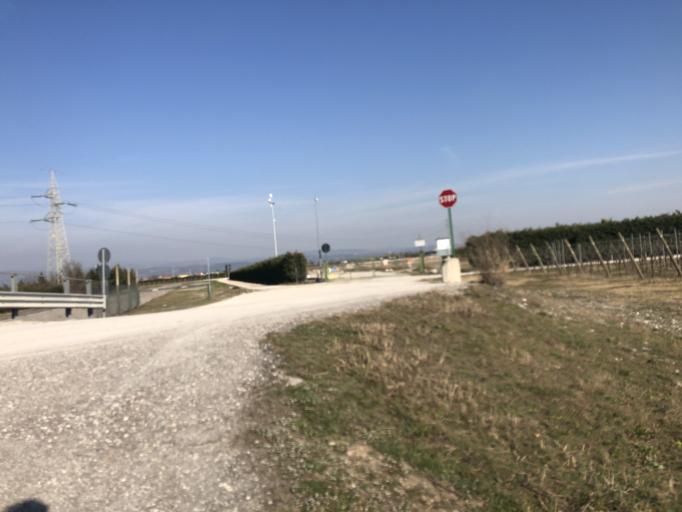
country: IT
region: Veneto
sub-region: Provincia di Verona
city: Lugagnano
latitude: 45.4214
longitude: 10.8815
